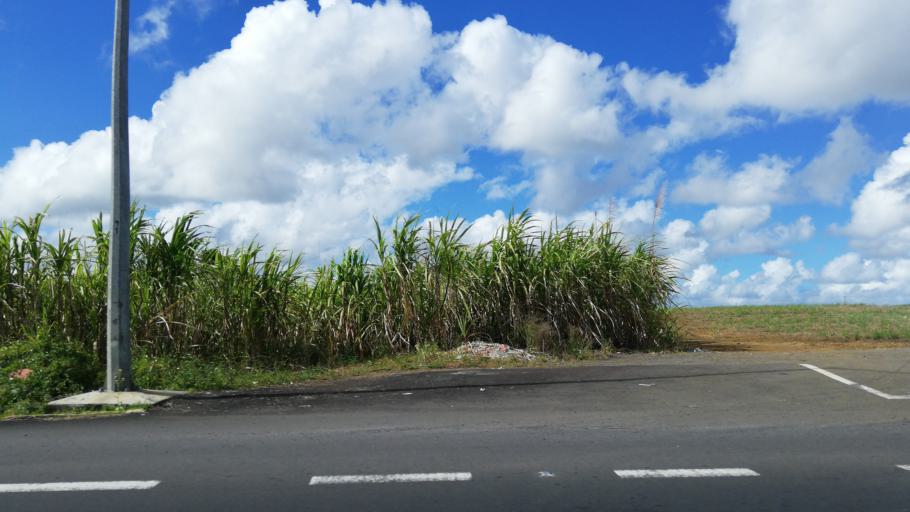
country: MU
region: Moka
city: Providence
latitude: -20.2381
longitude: 57.6259
